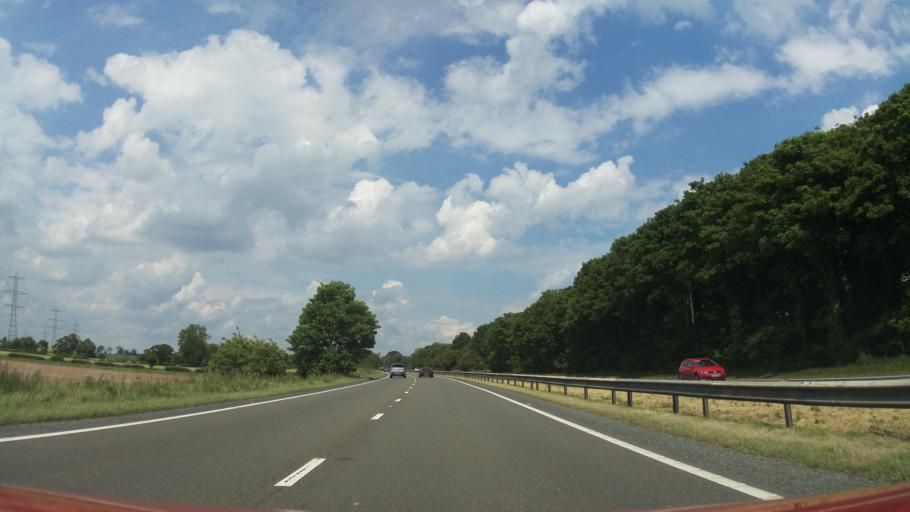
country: GB
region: England
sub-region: North Yorkshire
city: Thirsk
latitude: 54.2766
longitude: -1.3413
